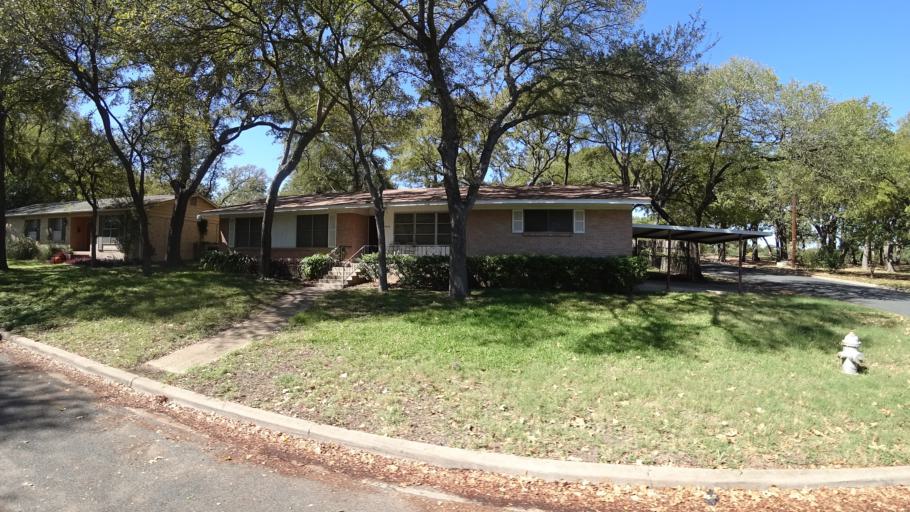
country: US
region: Texas
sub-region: Travis County
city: Austin
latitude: 30.2943
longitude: -97.7089
